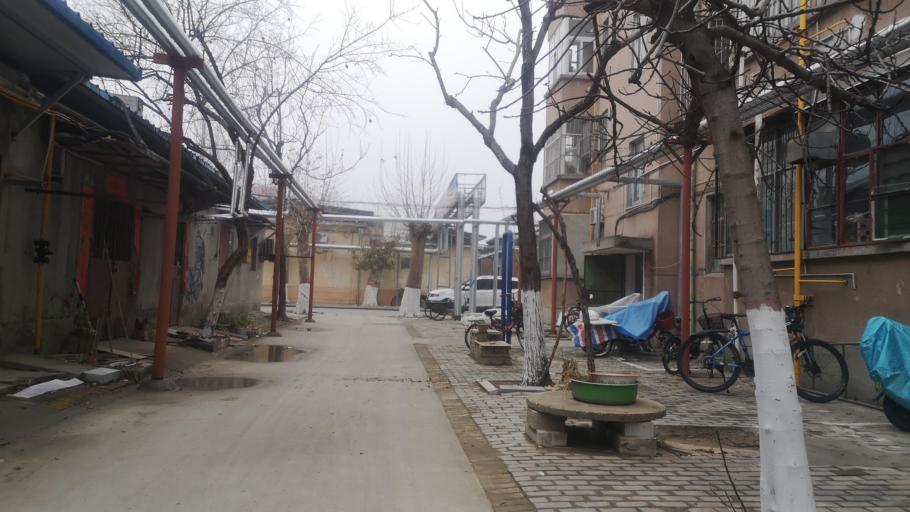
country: CN
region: Henan Sheng
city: Zhongyuanlu
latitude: 35.7635
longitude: 115.0716
